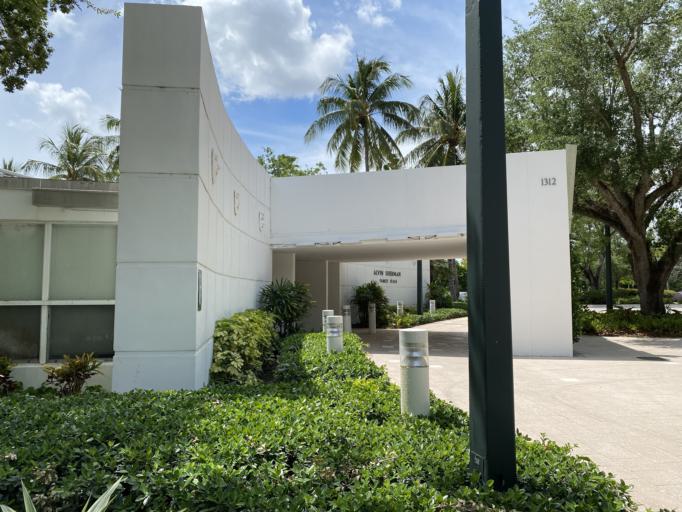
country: US
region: Florida
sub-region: Miami-Dade County
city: Coral Gables
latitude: 25.7199
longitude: -80.2798
